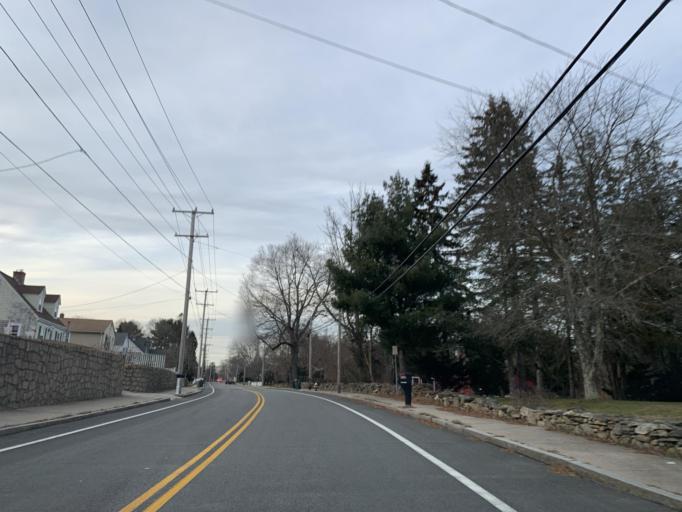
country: US
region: Rhode Island
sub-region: Providence County
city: Greenville
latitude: 41.8647
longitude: -71.5447
